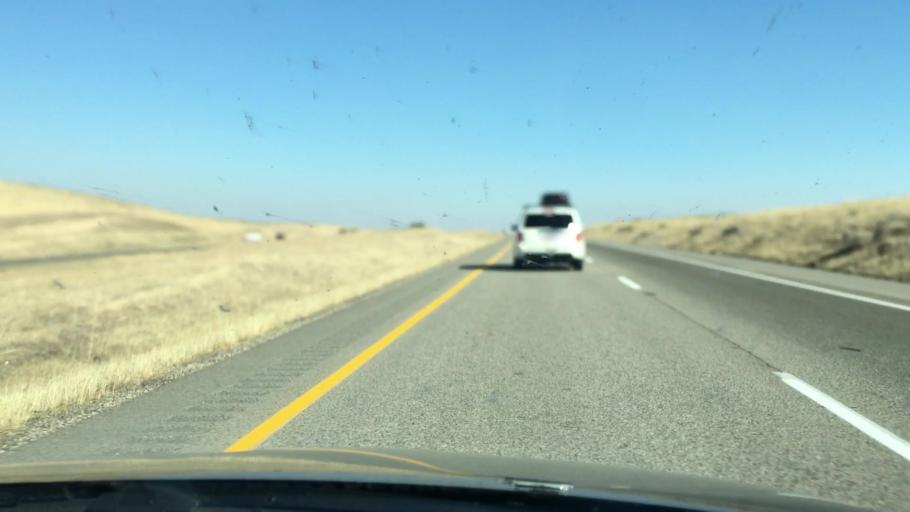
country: US
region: Idaho
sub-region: Ada County
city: Boise
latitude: 43.4860
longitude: -116.1195
